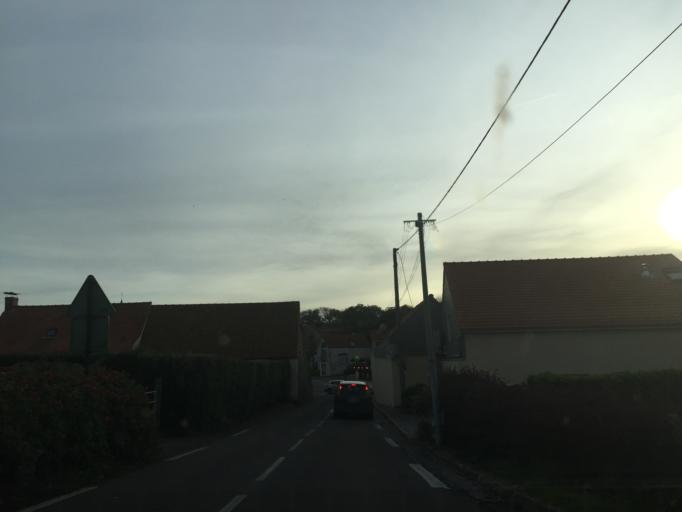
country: FR
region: Nord-Pas-de-Calais
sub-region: Departement du Pas-de-Calais
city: Sangatte
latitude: 50.9183
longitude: 1.7135
